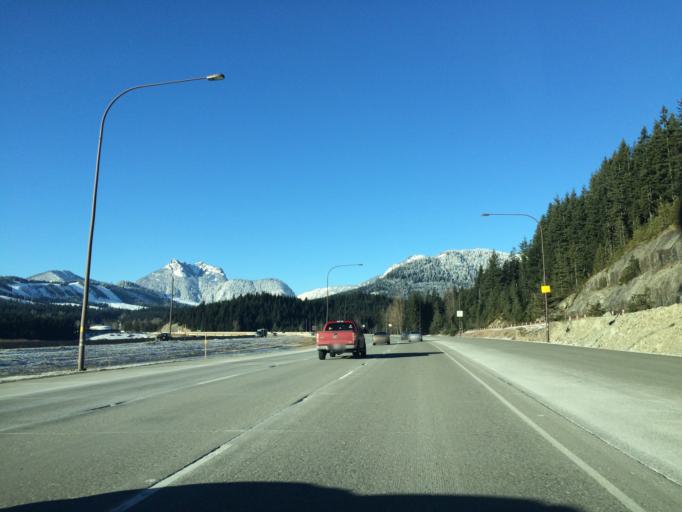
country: US
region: Washington
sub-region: King County
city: Tanner
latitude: 47.3861
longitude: -121.3788
